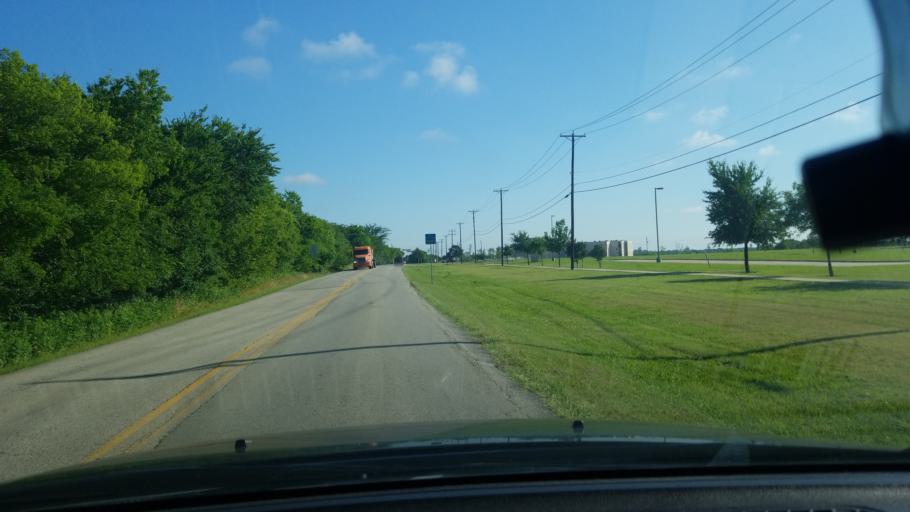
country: US
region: Texas
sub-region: Dallas County
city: Sunnyvale
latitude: 32.7986
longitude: -96.5610
